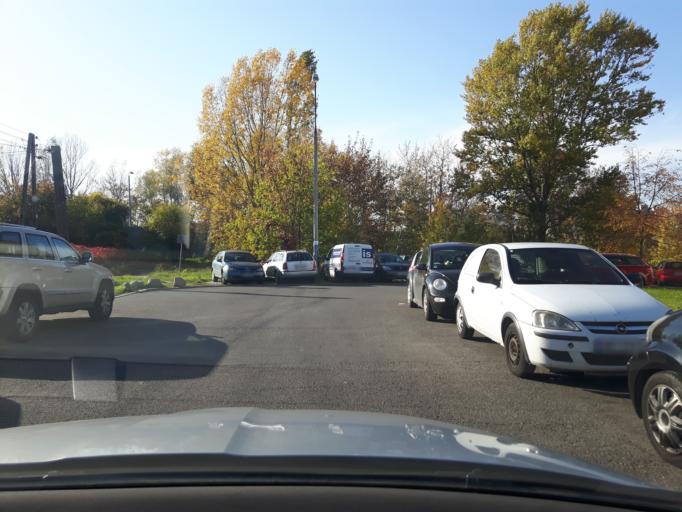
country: PL
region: Masovian Voivodeship
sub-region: Warszawa
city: Bemowo
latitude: 52.2342
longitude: 20.9245
